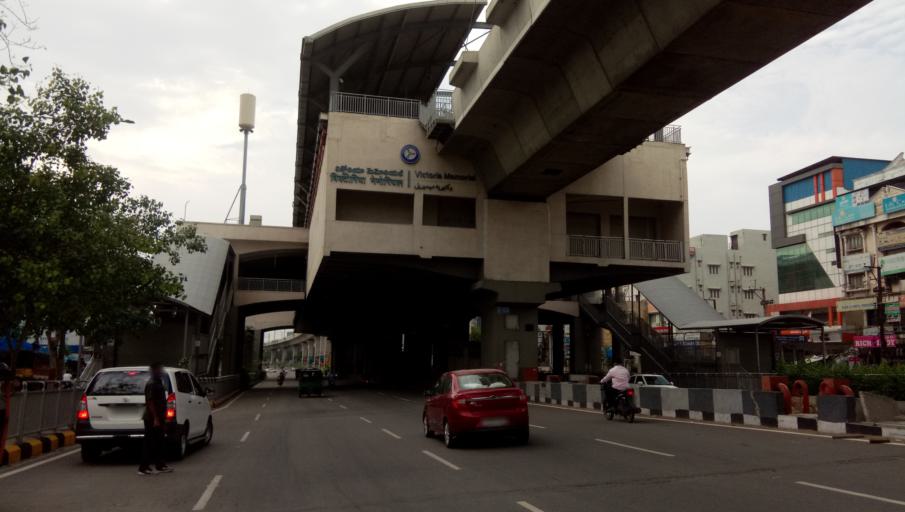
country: IN
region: Telangana
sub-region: Rangareddi
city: Lal Bahadur Nagar
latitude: 17.3608
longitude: 78.5441
